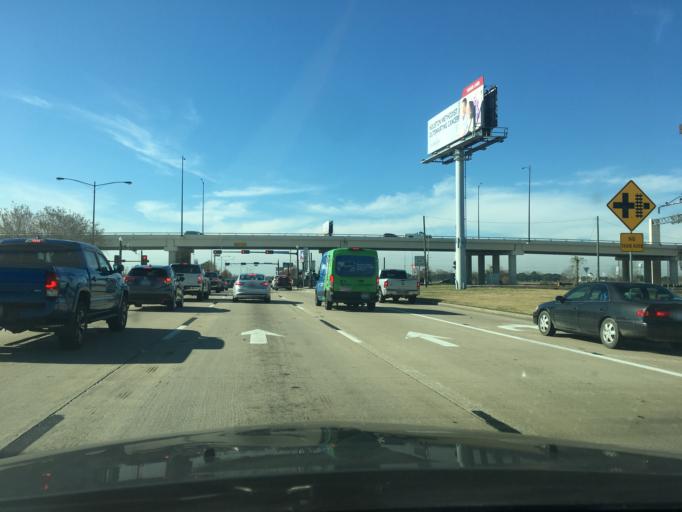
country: US
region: Texas
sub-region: Fort Bend County
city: Sugar Land
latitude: 29.6142
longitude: -95.6481
